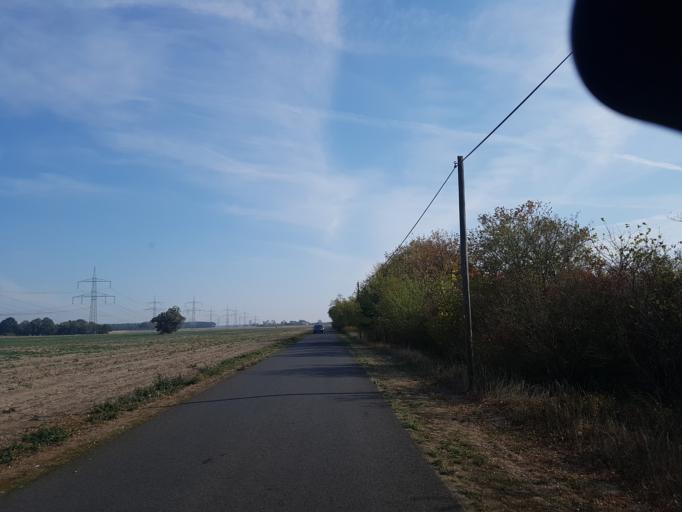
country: DE
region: Brandenburg
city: Ihlow
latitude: 51.8356
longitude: 13.3225
